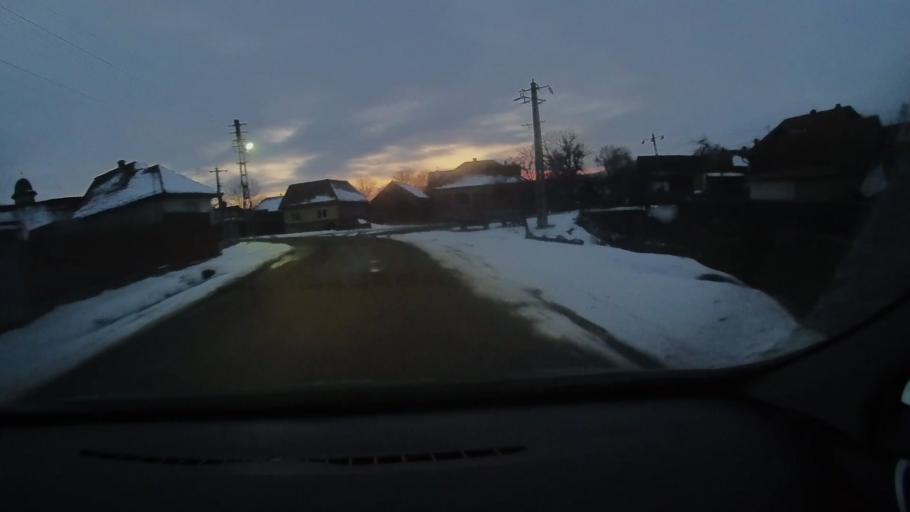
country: RO
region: Harghita
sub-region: Comuna Darjiu
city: Darjiu
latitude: 46.1732
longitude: 25.2344
